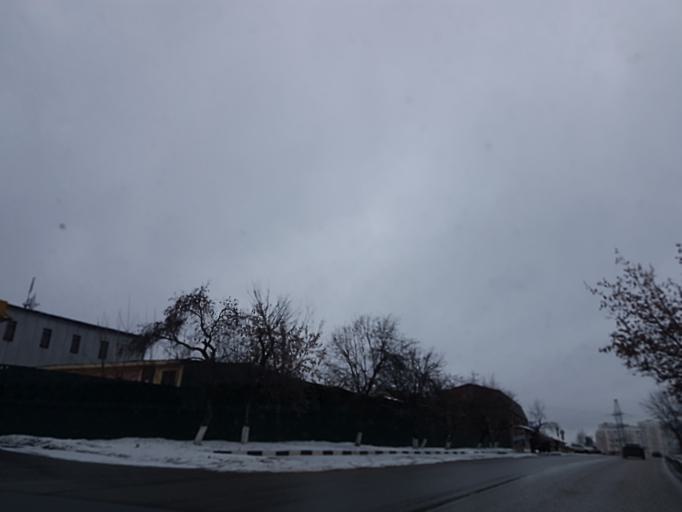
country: RU
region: Moskovskaya
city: Pavshino
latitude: 55.8228
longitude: 37.3562
